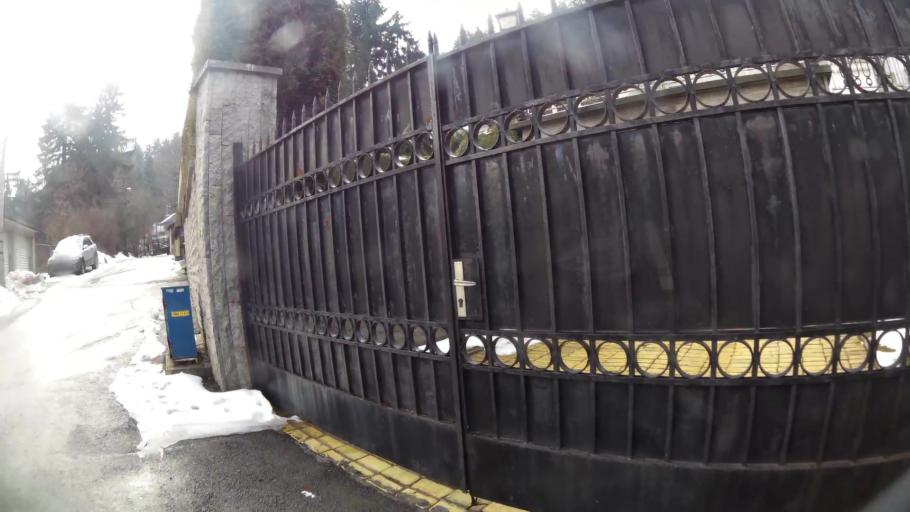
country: BG
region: Sofia-Capital
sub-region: Stolichna Obshtina
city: Sofia
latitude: 42.6427
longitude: 23.2785
